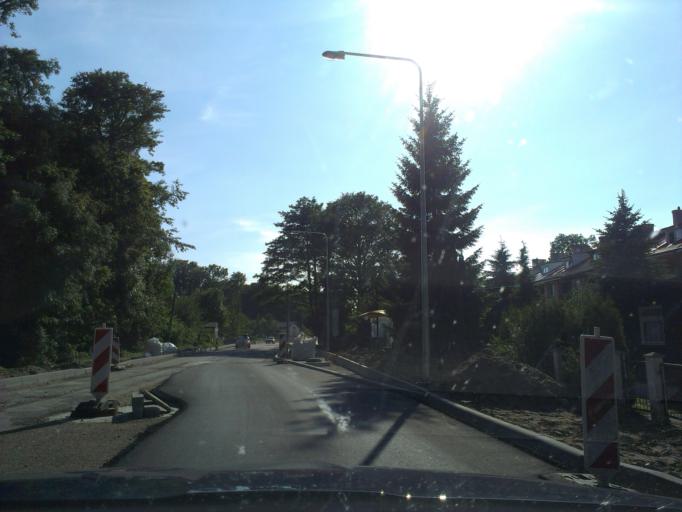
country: PL
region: West Pomeranian Voivodeship
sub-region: Powiat kamienski
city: Dziwnow
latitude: 54.0274
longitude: 14.7710
